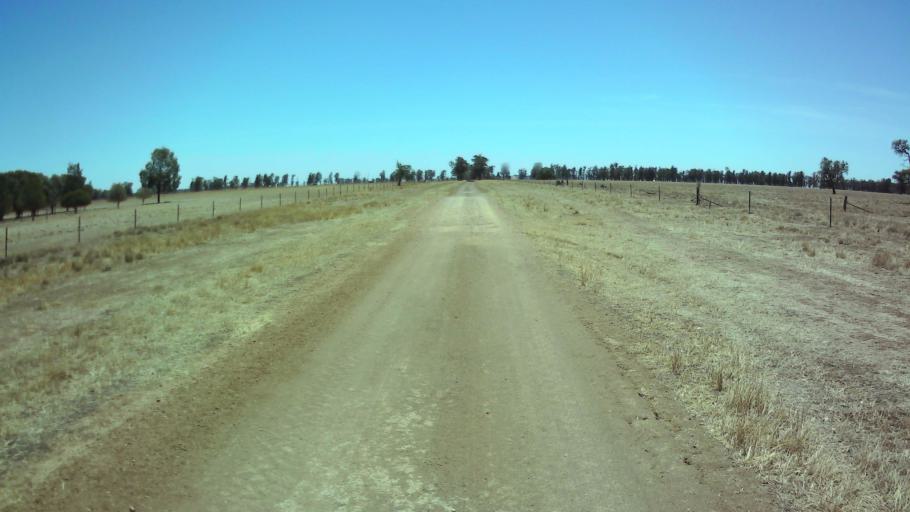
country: AU
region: New South Wales
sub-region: Weddin
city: Grenfell
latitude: -33.9771
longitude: 147.7369
